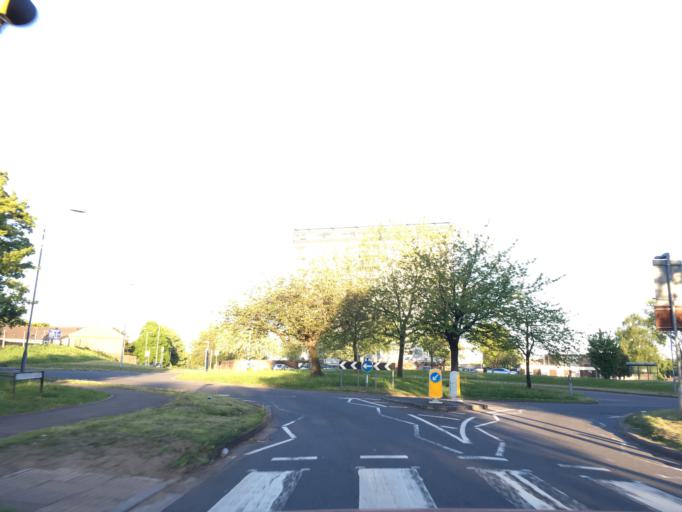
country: GB
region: Wales
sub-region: Newport
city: Llanwern
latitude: 51.5960
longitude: -2.9323
